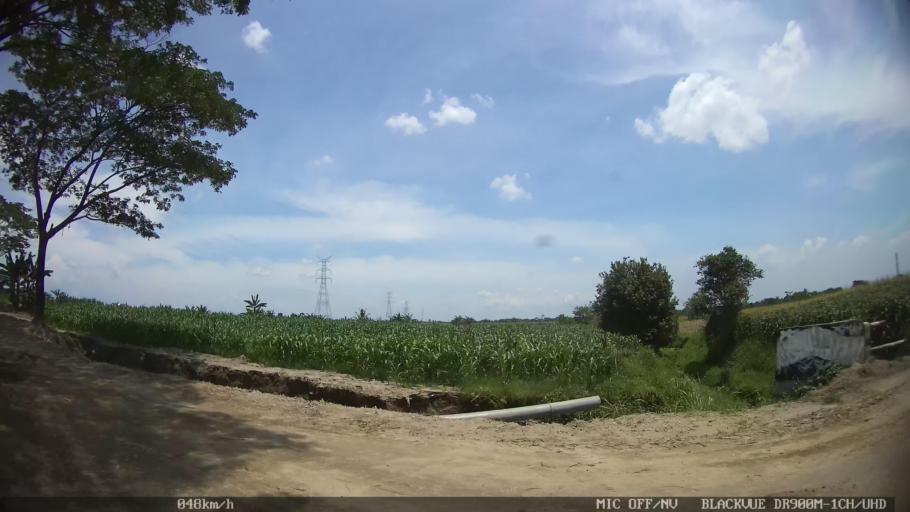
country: ID
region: North Sumatra
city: Binjai
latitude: 3.5911
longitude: 98.5154
